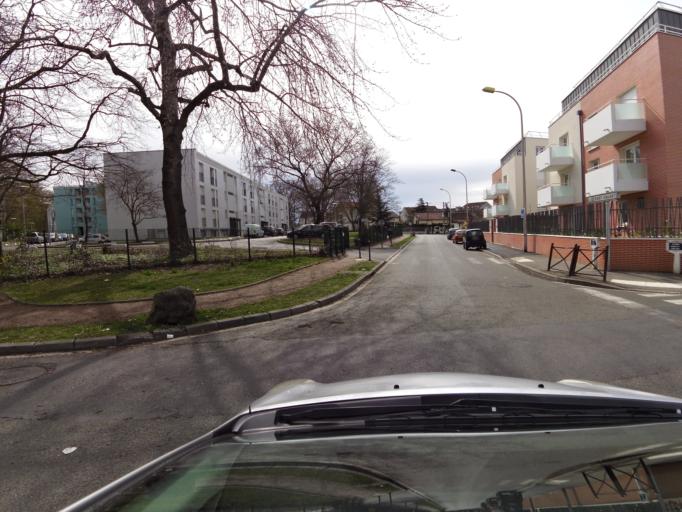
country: FR
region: Ile-de-France
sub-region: Departement de Seine-Saint-Denis
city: Tremblay-en-France
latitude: 48.9489
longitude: 2.5633
